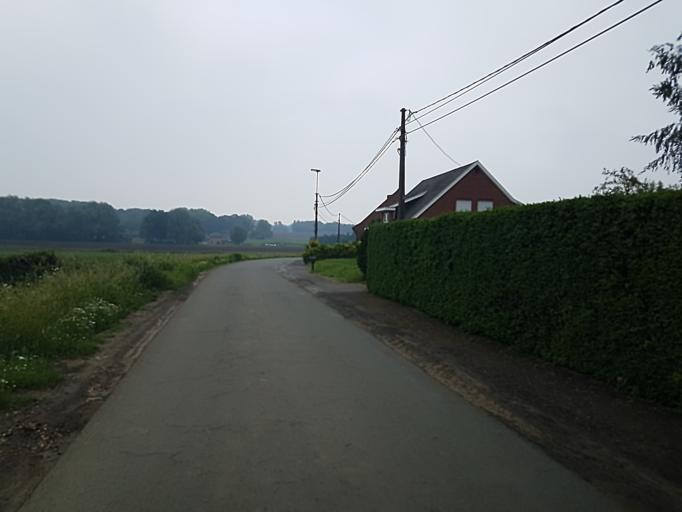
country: BE
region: Flanders
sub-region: Provincie West-Vlaanderen
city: Zonnebeke
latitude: 50.8522
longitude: 2.9622
